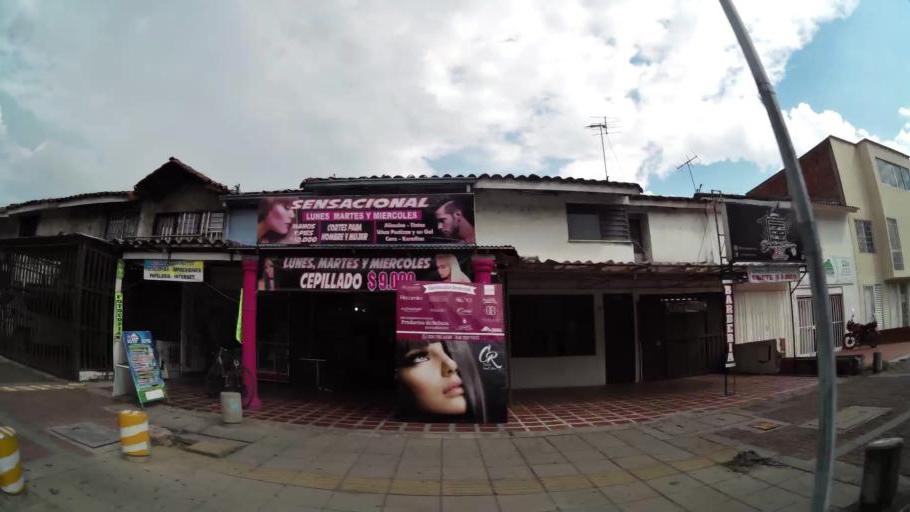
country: CO
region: Valle del Cauca
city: Cali
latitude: 3.4793
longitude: -76.5162
